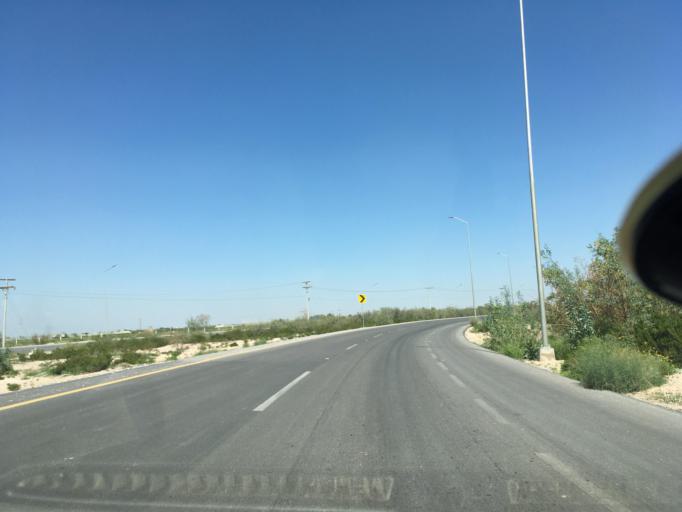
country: MX
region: Coahuila
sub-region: Torreon
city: Fraccionamiento la Noria
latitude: 25.4919
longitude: -103.3234
